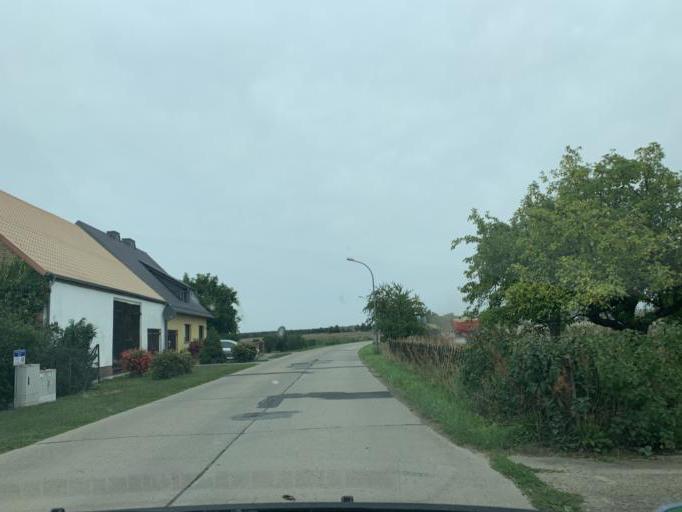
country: DE
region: Brandenburg
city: Zehdenick
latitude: 53.0084
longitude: 13.2757
